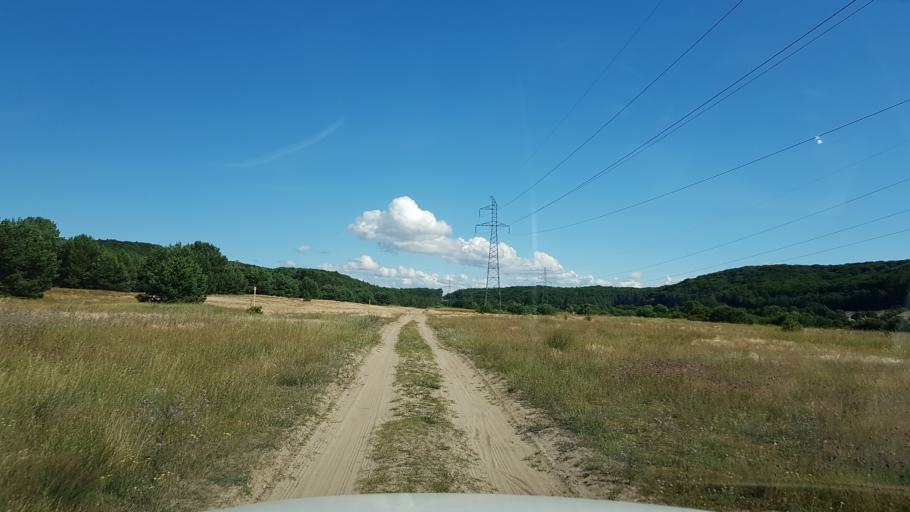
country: PL
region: West Pomeranian Voivodeship
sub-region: Powiat kamienski
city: Miedzyzdroje
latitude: 53.8857
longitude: 14.4407
